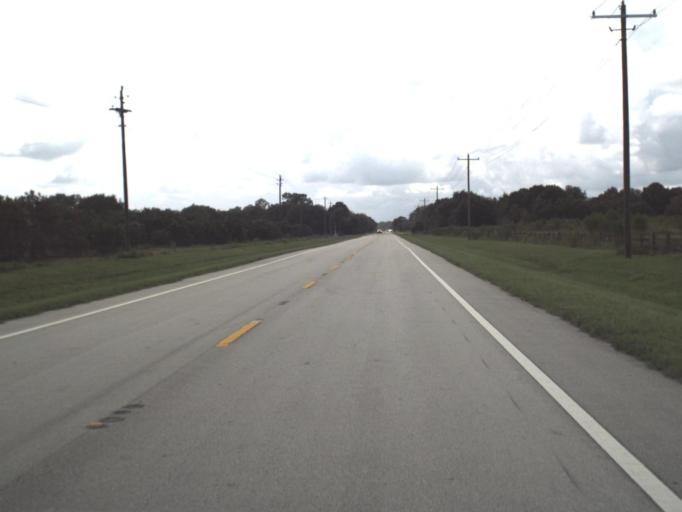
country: US
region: Florida
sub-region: DeSoto County
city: Nocatee
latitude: 27.2017
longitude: -81.9651
